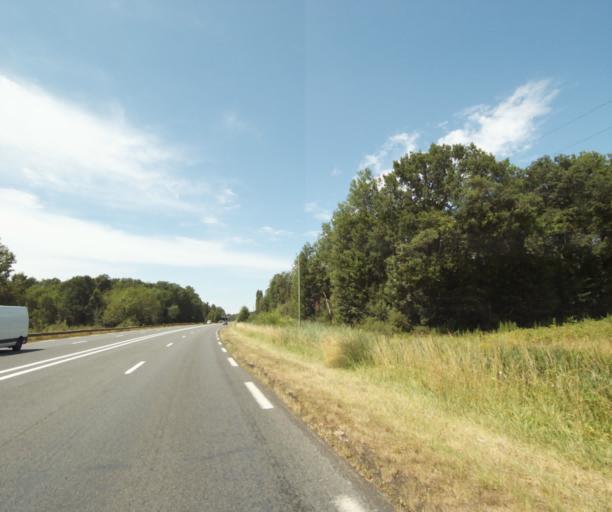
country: FR
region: Ile-de-France
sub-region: Departement de Seine-et-Marne
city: Cely
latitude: 48.4659
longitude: 2.5452
